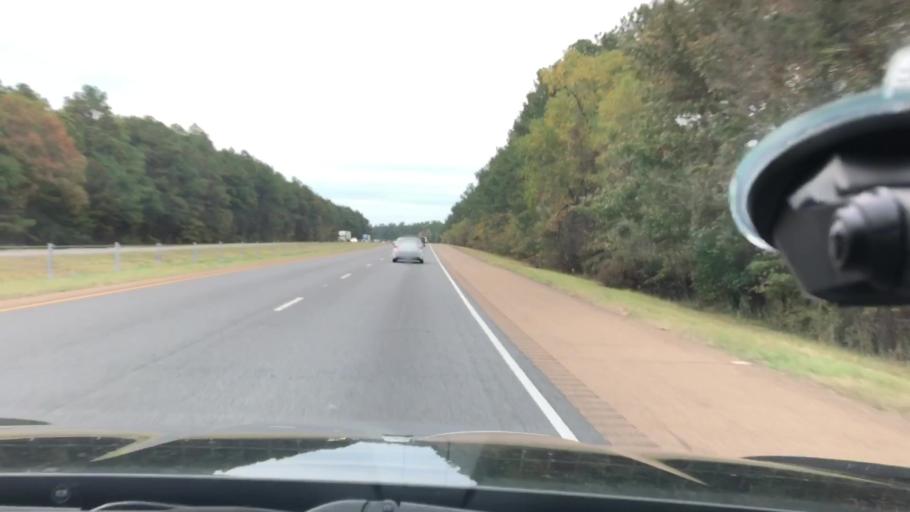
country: US
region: Arkansas
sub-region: Clark County
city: Gurdon
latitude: 33.9533
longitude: -93.2303
